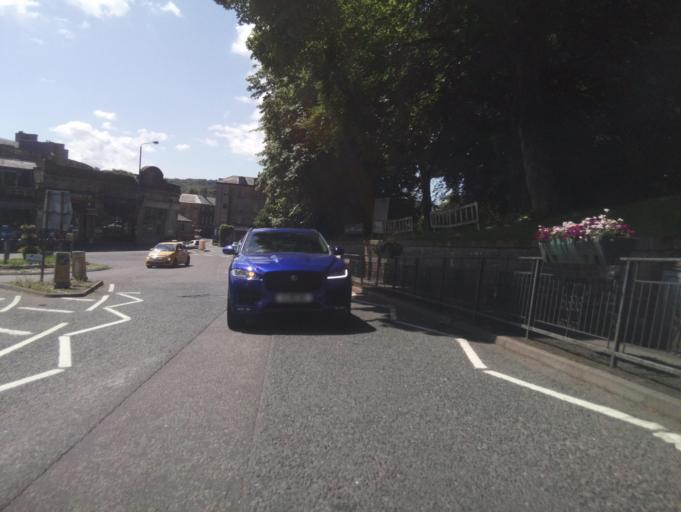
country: GB
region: England
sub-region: Derbyshire
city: Buxton
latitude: 53.2602
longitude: -1.9146
